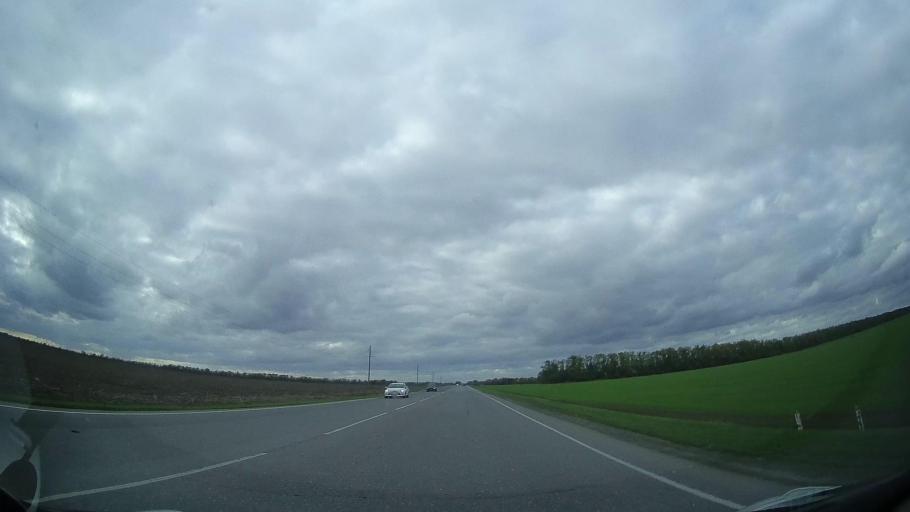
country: RU
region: Rostov
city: Mechetinskaya
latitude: 46.7896
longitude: 40.4005
